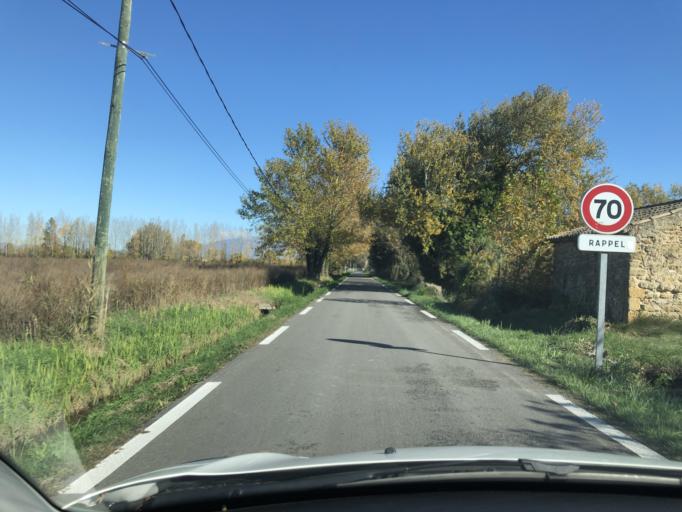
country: FR
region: Provence-Alpes-Cote d'Azur
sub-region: Departement du Vaucluse
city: Althen-des-Paluds
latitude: 43.9814
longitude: 4.9508
